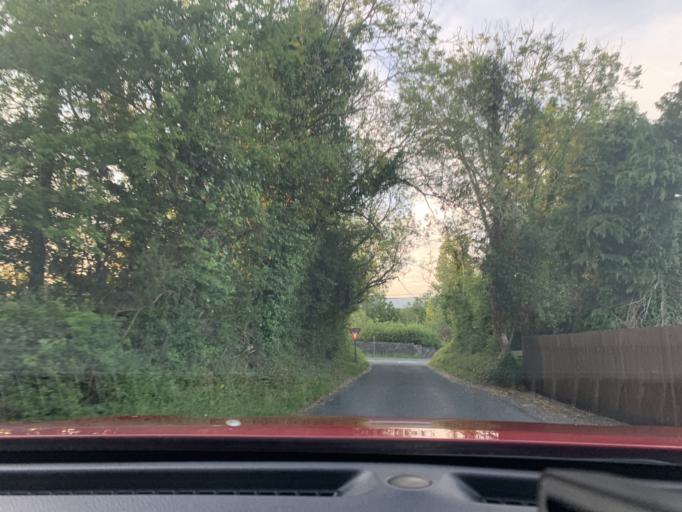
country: IE
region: Connaught
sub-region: Sligo
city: Sligo
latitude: 54.2905
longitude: -8.4307
